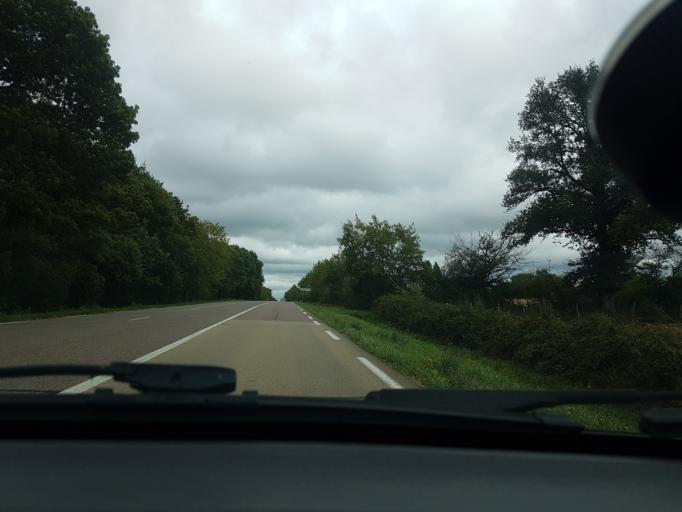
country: FR
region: Bourgogne
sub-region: Departement de la Cote-d'Or
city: Saulieu
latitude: 47.4288
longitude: 4.1033
